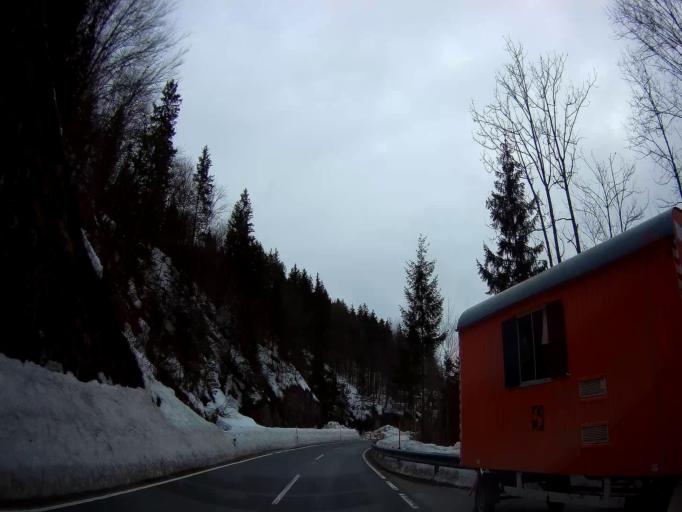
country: AT
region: Salzburg
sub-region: Politischer Bezirk Hallein
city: Krispl
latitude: 47.7503
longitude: 13.1745
